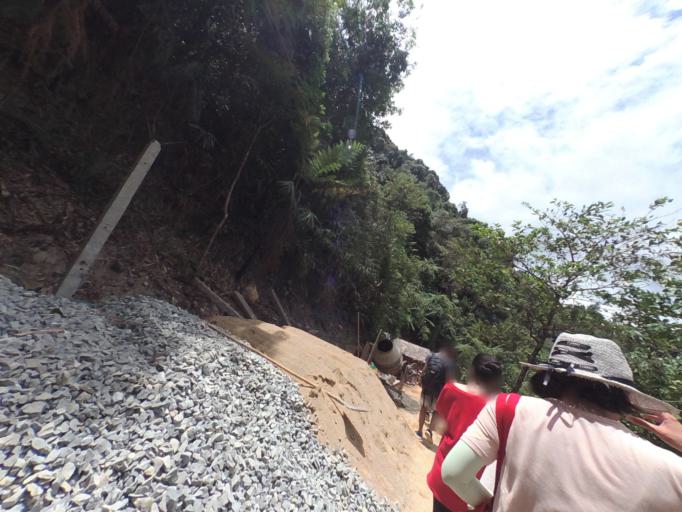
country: VN
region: Thua Thien-Hue
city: A Luoi
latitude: 16.3081
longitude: 107.2169
